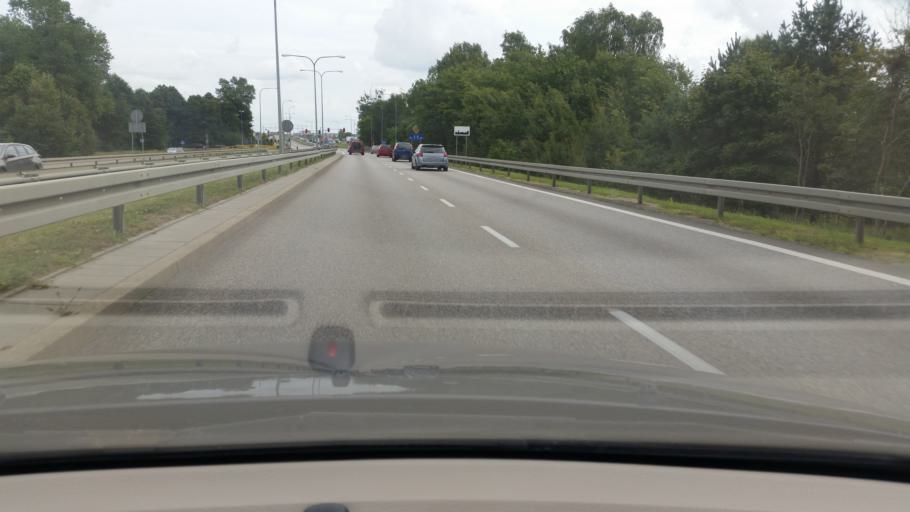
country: PL
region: Pomeranian Voivodeship
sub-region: Powiat wejherowski
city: Wejherowo
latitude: 54.6083
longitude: 18.2084
